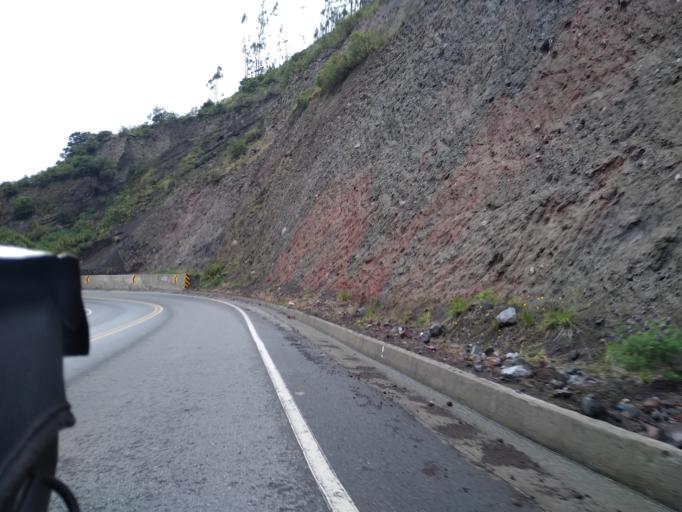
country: EC
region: Tungurahua
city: Banos
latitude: -1.5044
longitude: -78.5186
